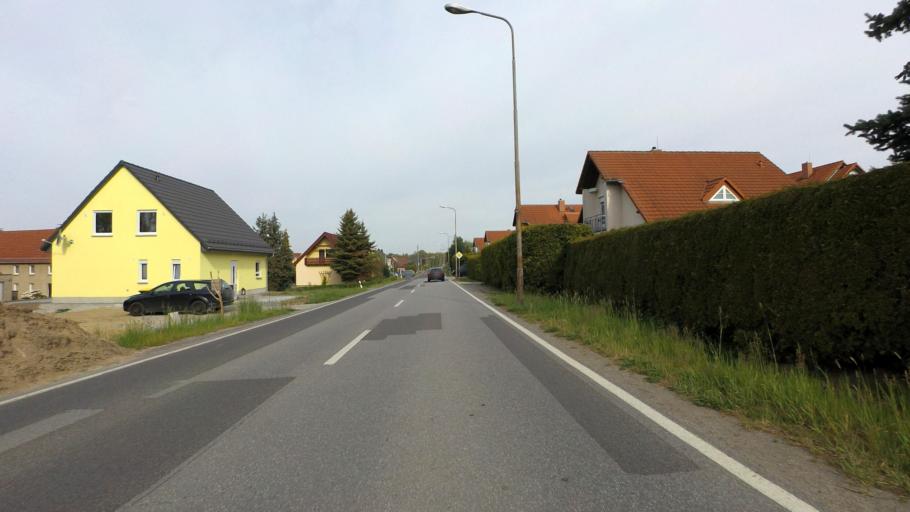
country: DE
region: Saxony
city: Arnsdorf
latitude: 51.0876
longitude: 14.0149
